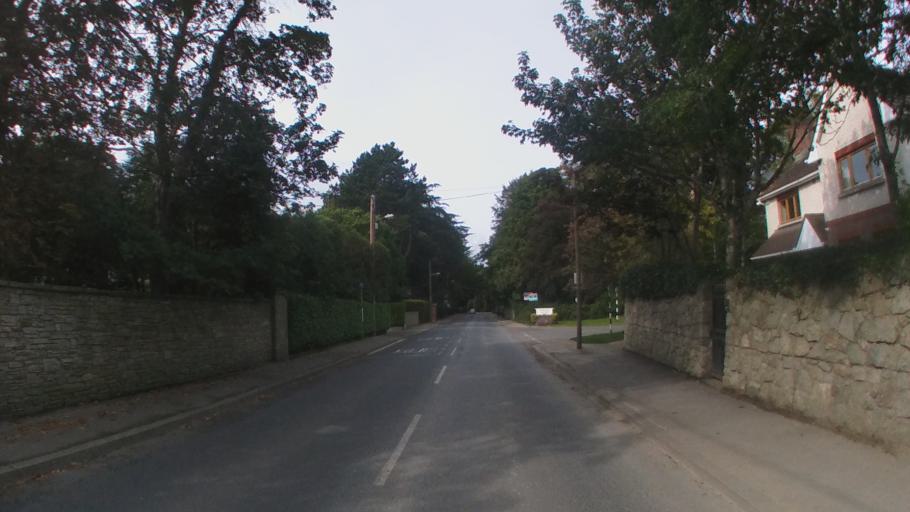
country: IE
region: Leinster
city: Foxrock
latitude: 53.2621
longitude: -6.1799
